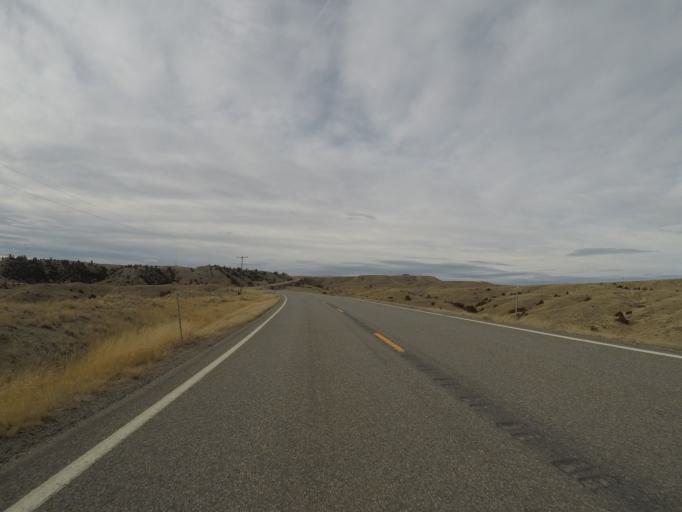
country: US
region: Montana
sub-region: Yellowstone County
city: Laurel
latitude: 45.8517
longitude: -108.7502
